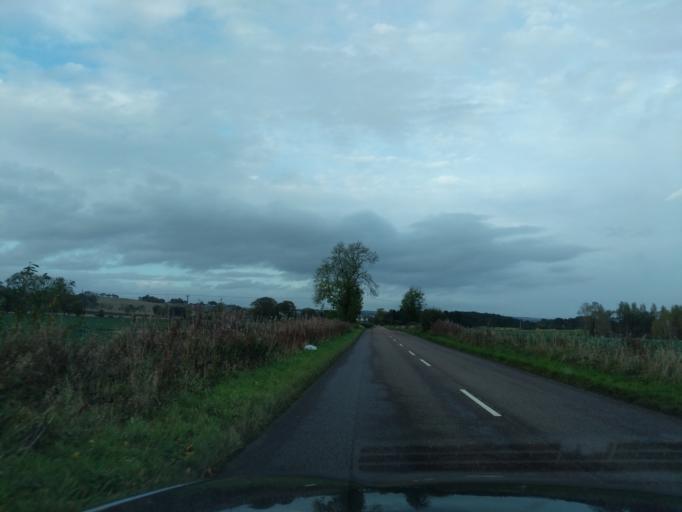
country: GB
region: Scotland
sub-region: Fife
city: Tayport
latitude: 56.4314
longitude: -2.8864
